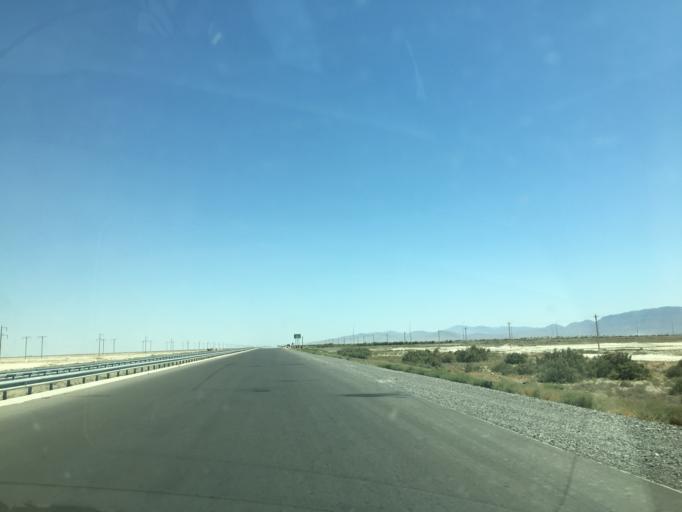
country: TM
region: Balkan
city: Serdar
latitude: 39.0611
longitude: 56.1020
